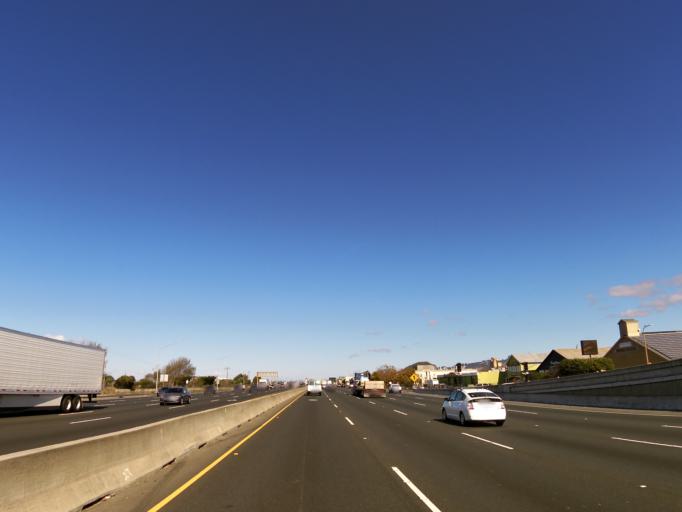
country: US
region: California
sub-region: Alameda County
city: Albany
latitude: 37.8674
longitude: -122.3039
